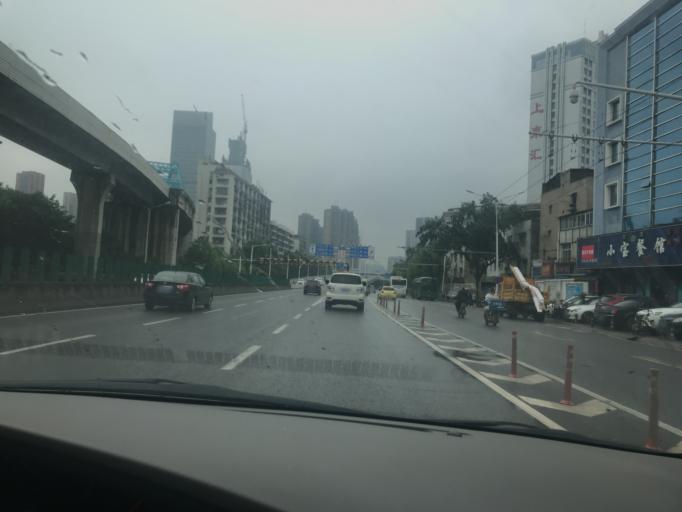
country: CN
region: Hubei
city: Jiang'an
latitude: 30.6190
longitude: 114.3073
